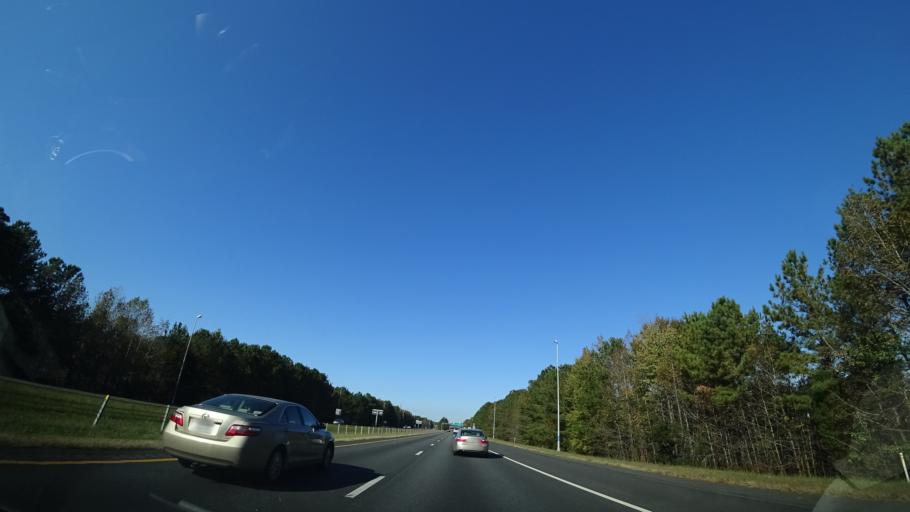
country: US
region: Virginia
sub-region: City of Portsmouth
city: Portsmouth Heights
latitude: 36.8090
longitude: -76.4306
